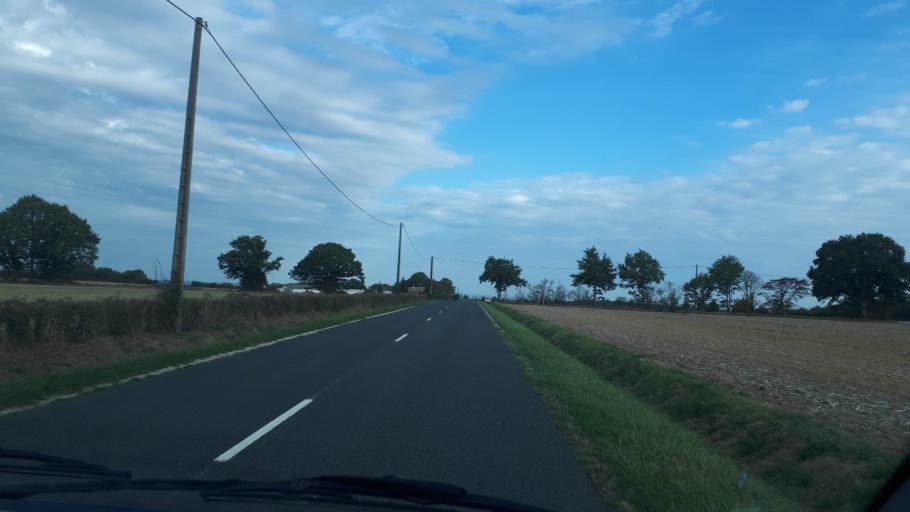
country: FR
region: Centre
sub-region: Departement du Loir-et-Cher
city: Mondoubleau
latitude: 47.9484
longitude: 0.9322
